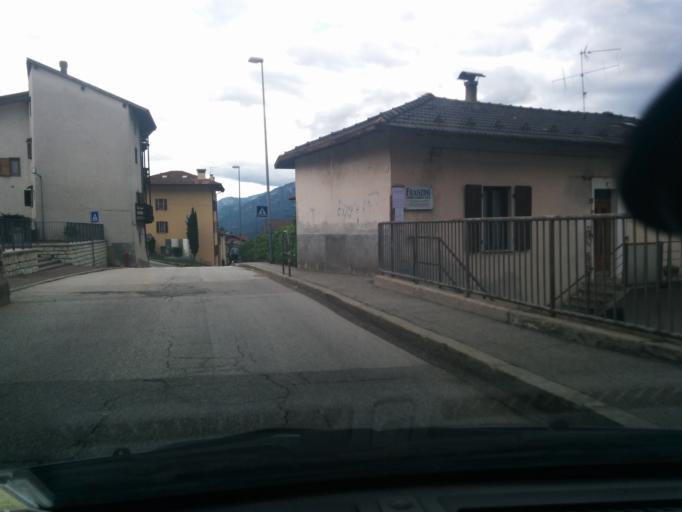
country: IT
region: Trentino-Alto Adige
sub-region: Provincia di Trento
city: Trento
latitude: 46.0890
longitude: 11.1307
